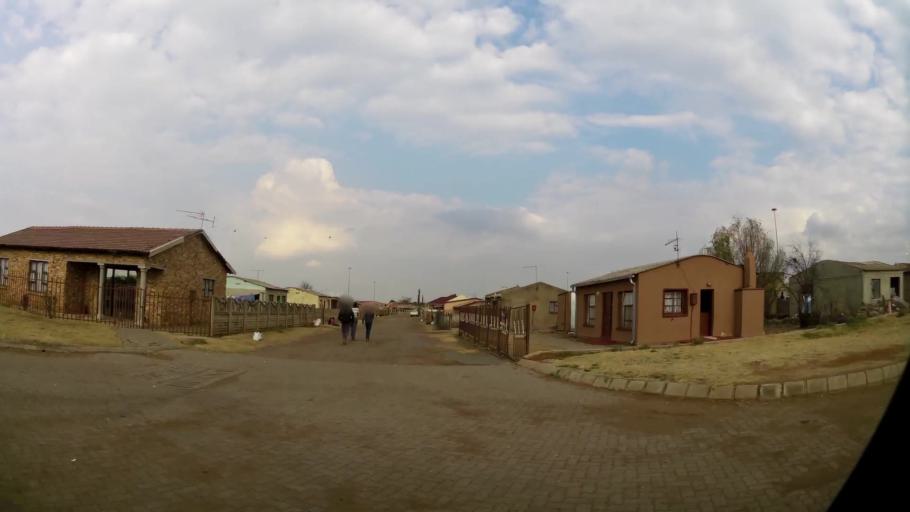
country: ZA
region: Gauteng
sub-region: Sedibeng District Municipality
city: Vereeniging
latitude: -26.6756
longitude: 27.8770
